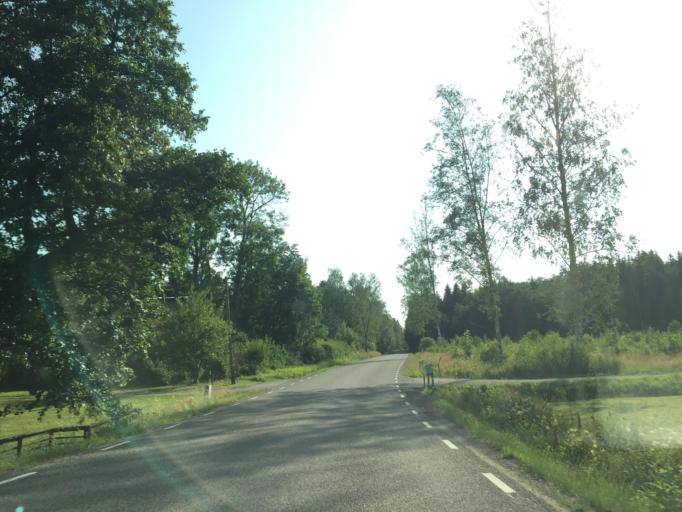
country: SE
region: Vaestra Goetaland
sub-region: Trollhattan
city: Sjuntorp
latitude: 58.2356
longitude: 12.1759
